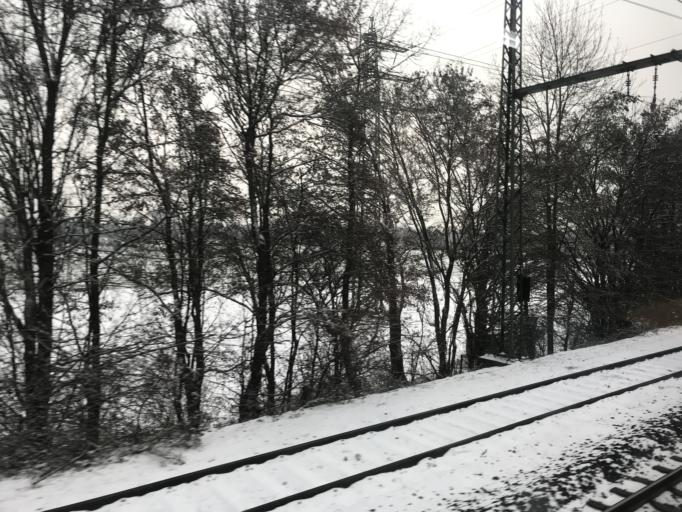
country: DE
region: Hesse
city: Kelsterbach
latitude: 50.0916
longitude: 8.5117
